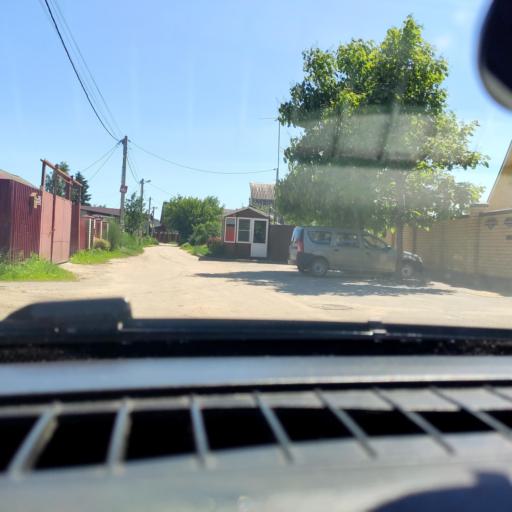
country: RU
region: Voronezj
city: Podgornoye
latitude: 51.7975
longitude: 39.1395
